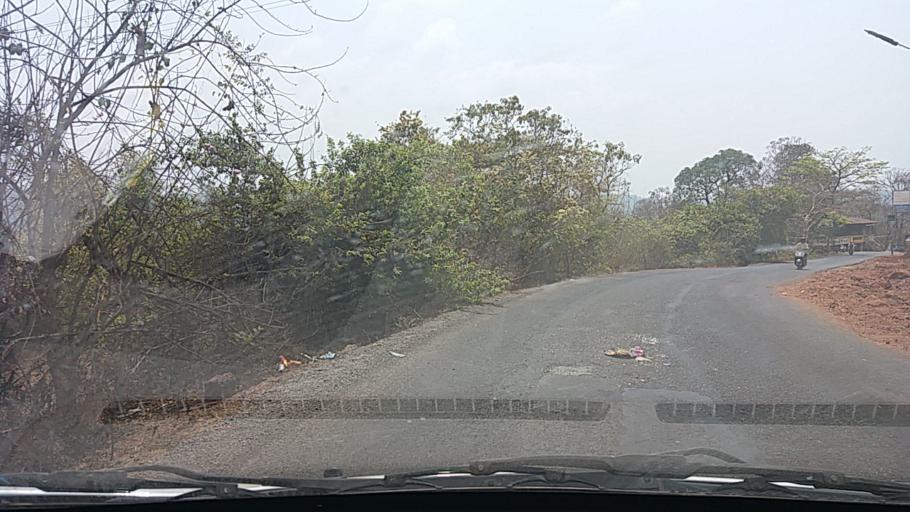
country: IN
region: Goa
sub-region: North Goa
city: Saligao
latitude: 15.5307
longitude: 73.7997
